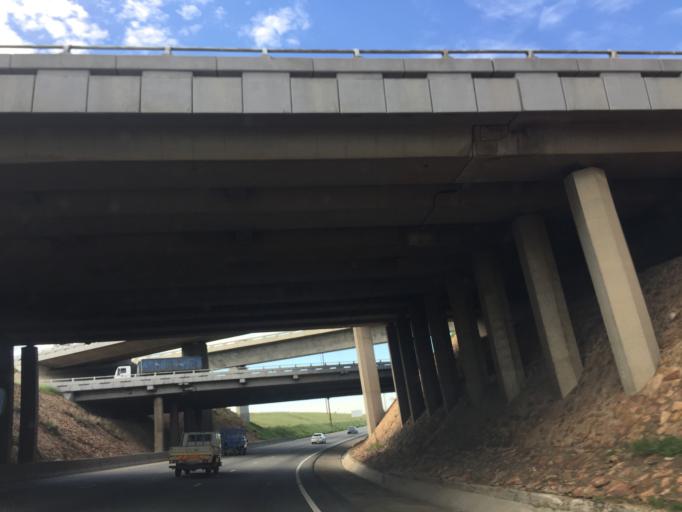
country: ZA
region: Gauteng
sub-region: Ekurhuleni Metropolitan Municipality
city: Germiston
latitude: -26.2395
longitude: 28.1266
